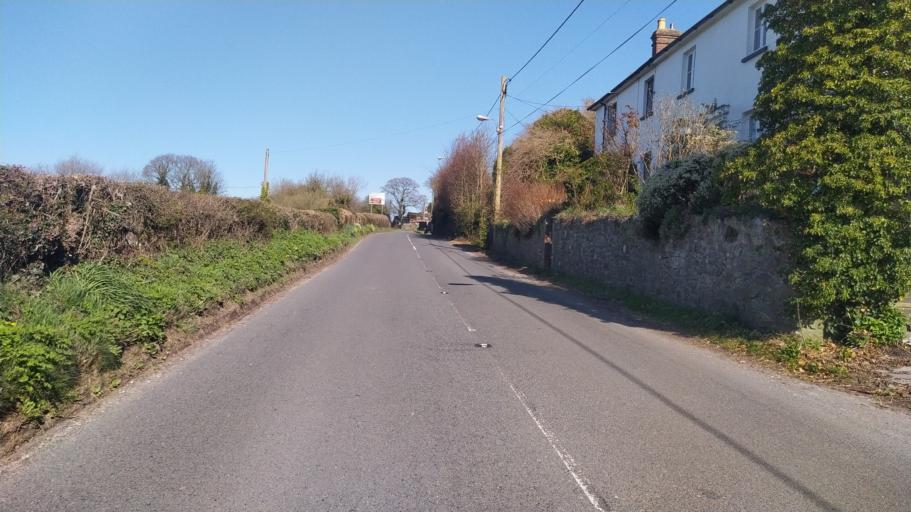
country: GB
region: England
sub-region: Dorset
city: Shaftesbury
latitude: 51.0038
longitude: -2.1299
